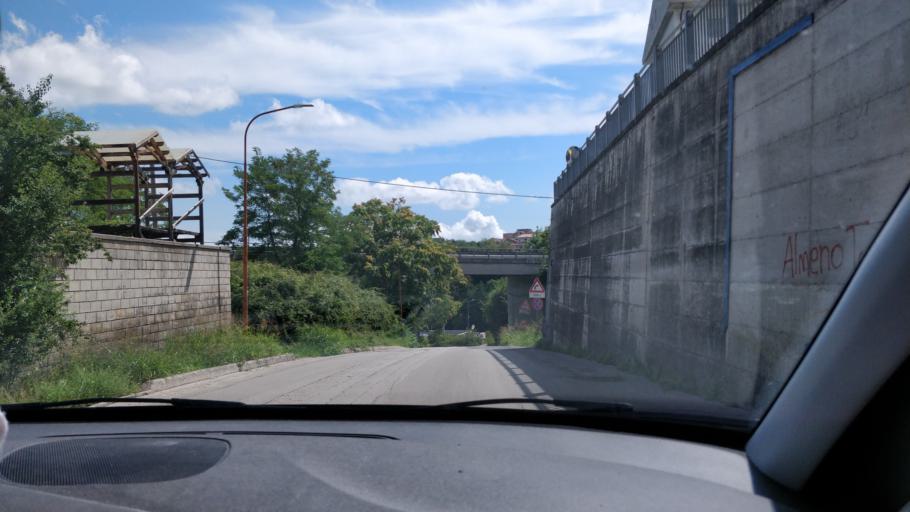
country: IT
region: Abruzzo
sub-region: Provincia di Chieti
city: Lanciano
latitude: 42.2292
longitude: 14.4005
